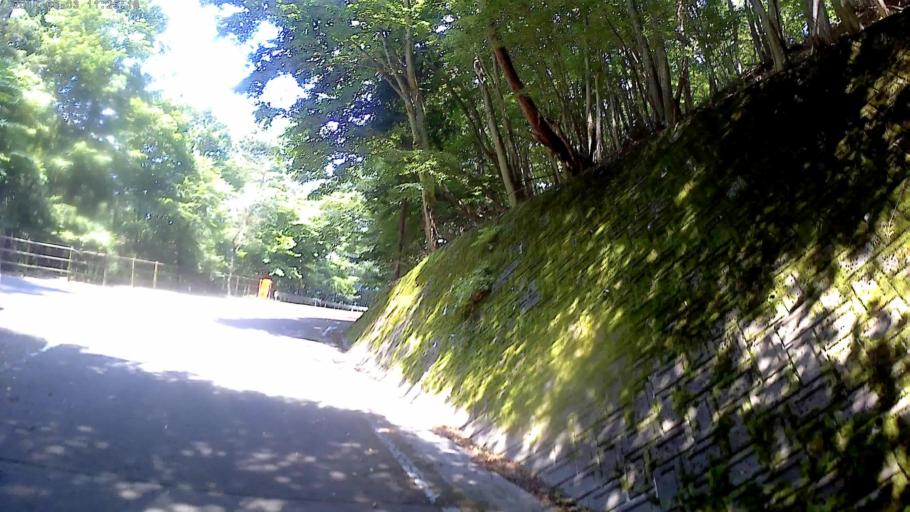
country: JP
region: Yamanashi
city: Enzan
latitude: 35.6136
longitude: 138.7785
